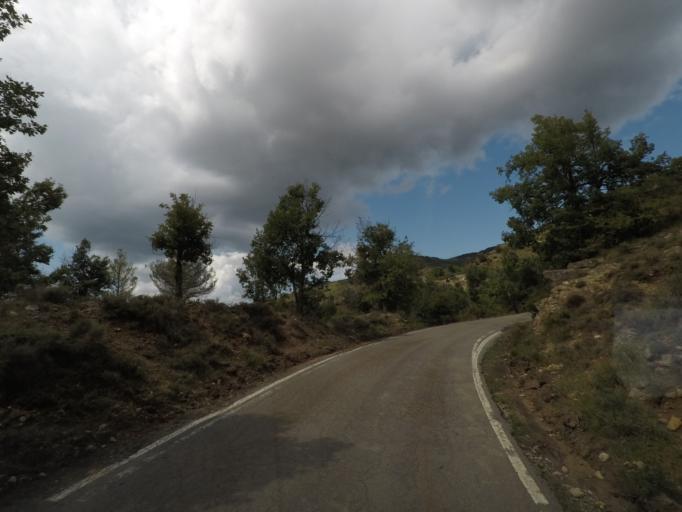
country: ES
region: Aragon
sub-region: Provincia de Huesca
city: Fiscal
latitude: 42.4109
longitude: -0.1153
